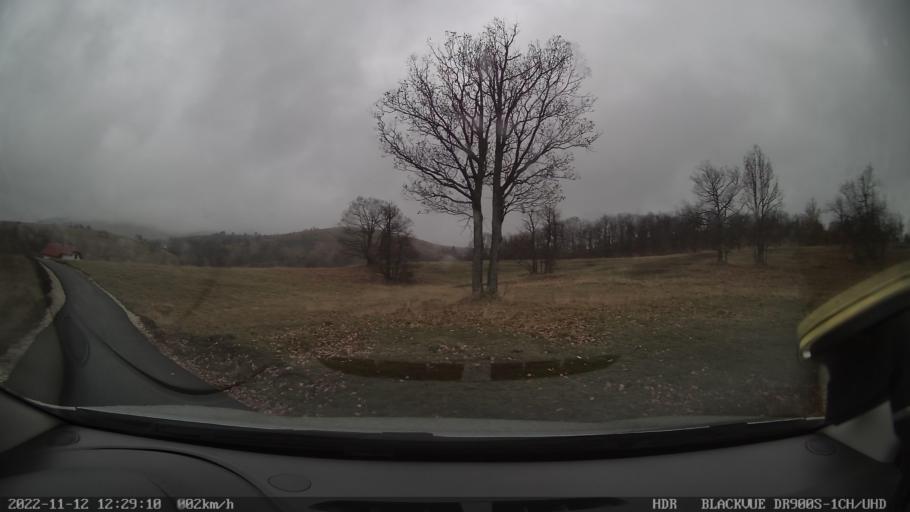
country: RS
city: Zlatibor
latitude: 43.7047
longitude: 19.7173
